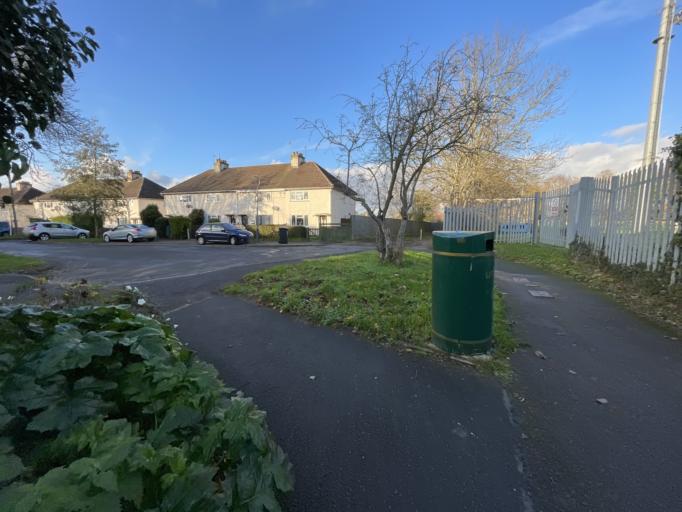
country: GB
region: England
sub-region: Warwickshire
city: Rugby
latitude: 52.3697
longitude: -1.2788
